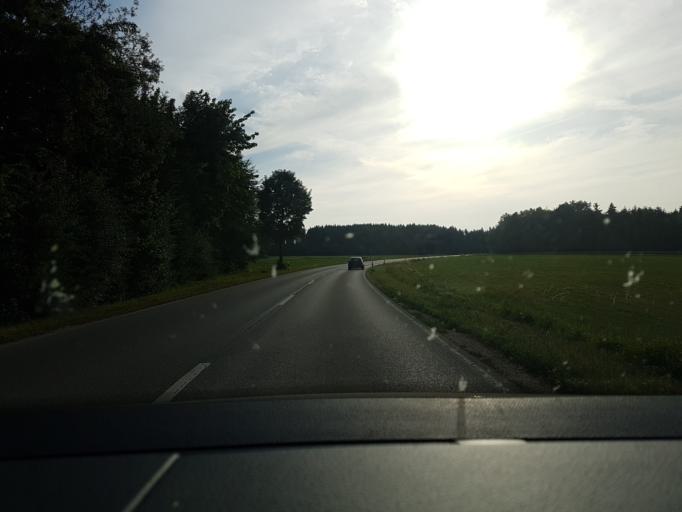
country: DE
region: Bavaria
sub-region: Upper Bavaria
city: Teisendorf
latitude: 47.8448
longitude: 12.8557
